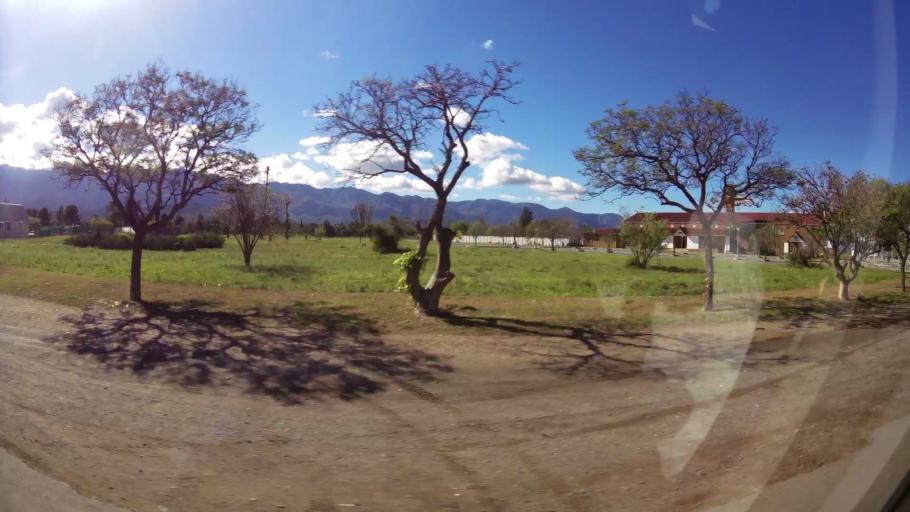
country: ZA
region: Western Cape
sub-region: Cape Winelands District Municipality
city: Ashton
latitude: -33.8127
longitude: 19.8923
